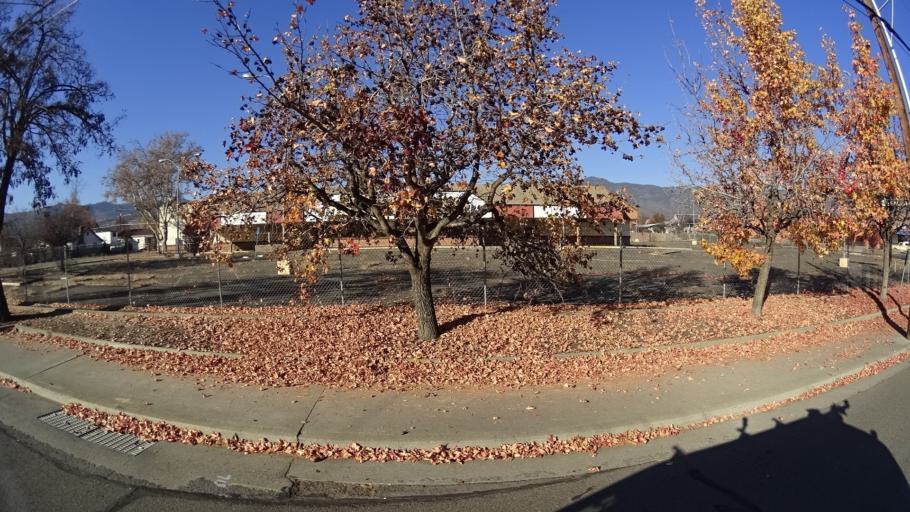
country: US
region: California
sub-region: Siskiyou County
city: Yreka
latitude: 41.7243
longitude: -122.6389
